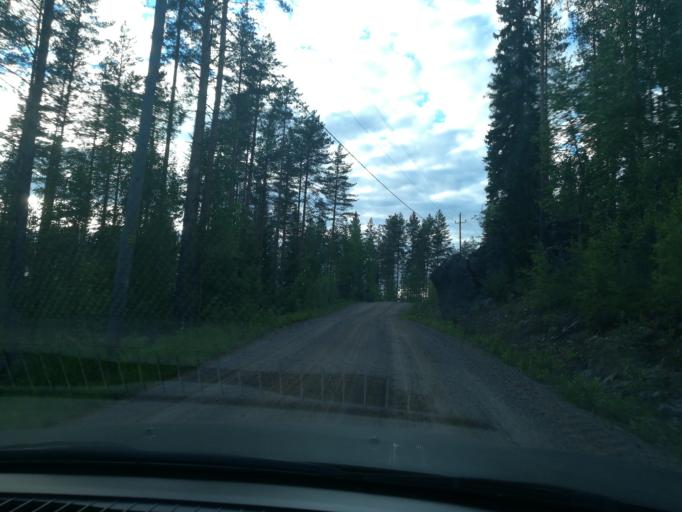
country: FI
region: Southern Savonia
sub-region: Mikkeli
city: Puumala
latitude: 61.5971
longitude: 28.1488
